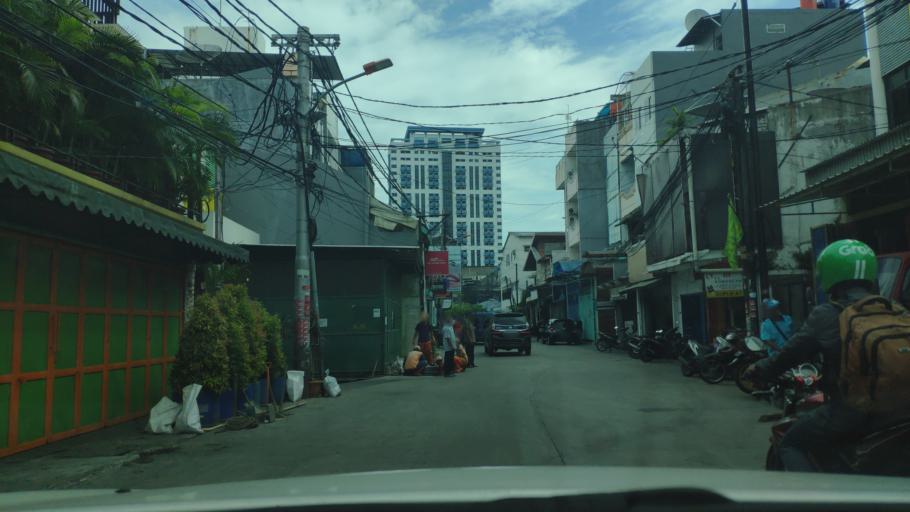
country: ID
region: Jakarta Raya
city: Jakarta
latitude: -6.1487
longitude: 106.8186
